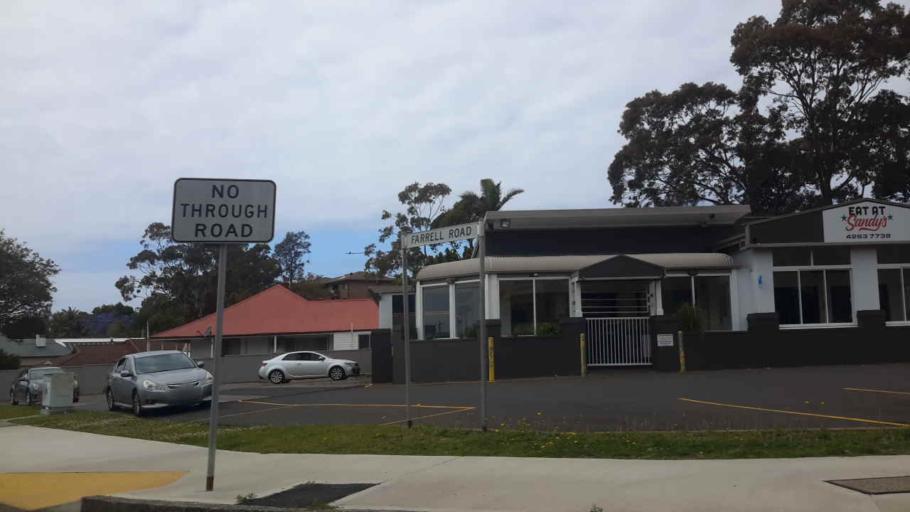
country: AU
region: New South Wales
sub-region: Wollongong
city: Bulli
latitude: -34.3383
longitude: 150.9096
